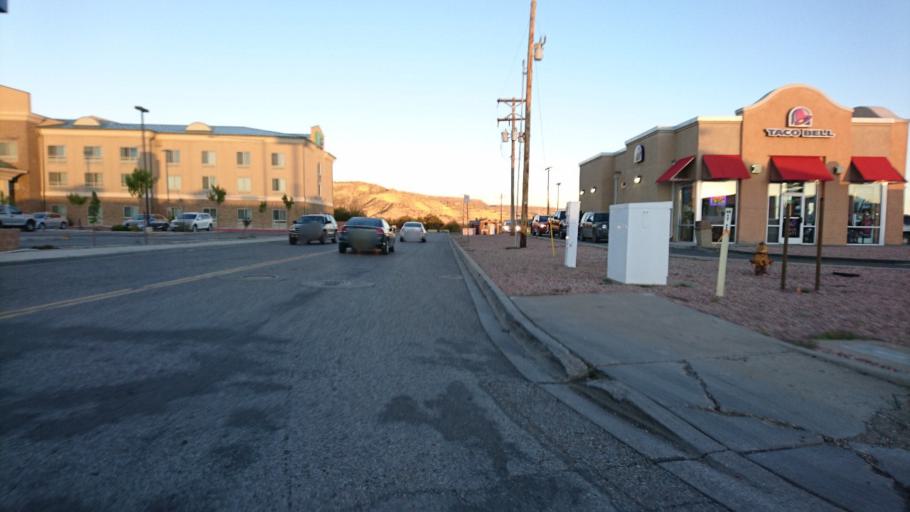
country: US
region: New Mexico
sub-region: Cibola County
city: Grants
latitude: 35.1286
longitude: -107.8273
